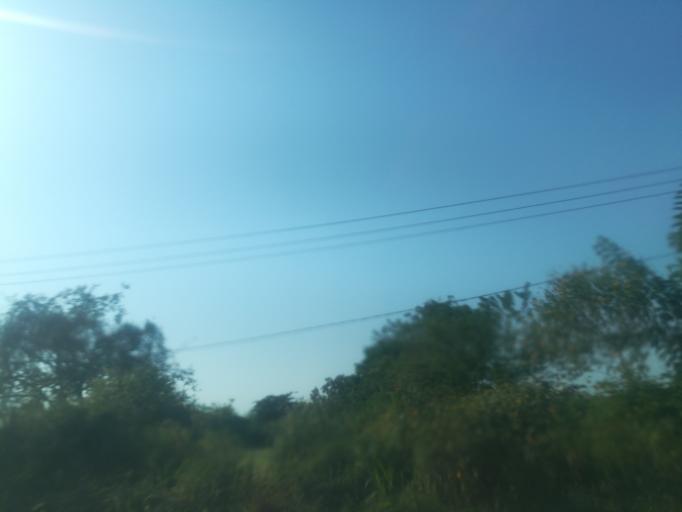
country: NG
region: Ogun
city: Abeokuta
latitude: 7.1803
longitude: 3.2791
